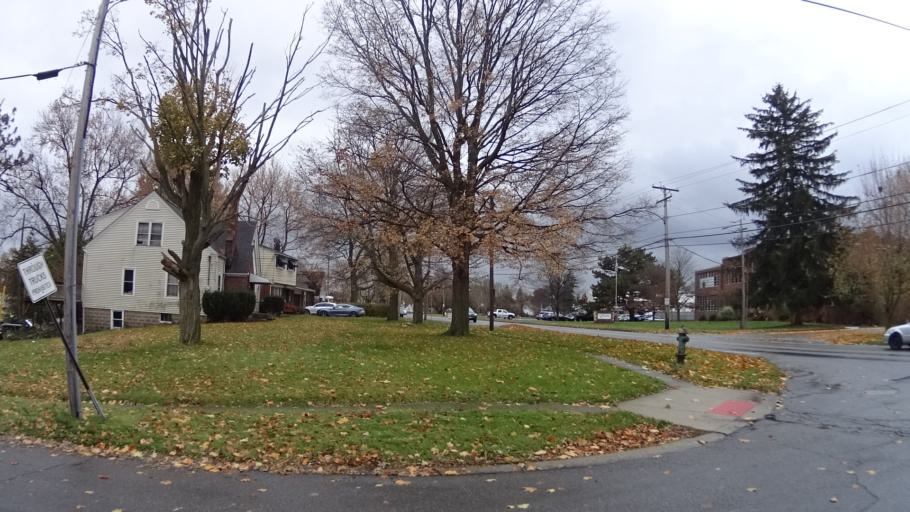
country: US
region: Ohio
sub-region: Lorain County
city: Elyria
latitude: 41.3874
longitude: -82.1292
